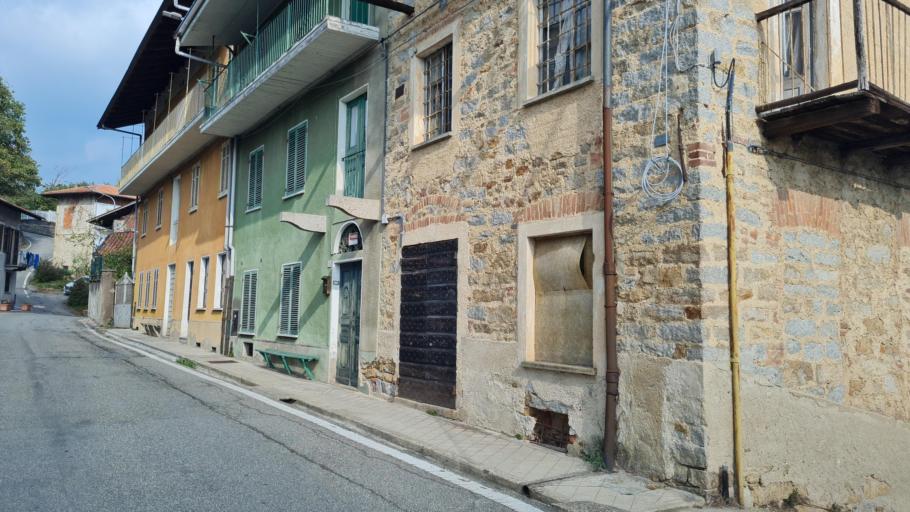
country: IT
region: Piedmont
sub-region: Provincia di Biella
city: Mezzana Mortigliengo
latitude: 45.6261
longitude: 8.1897
